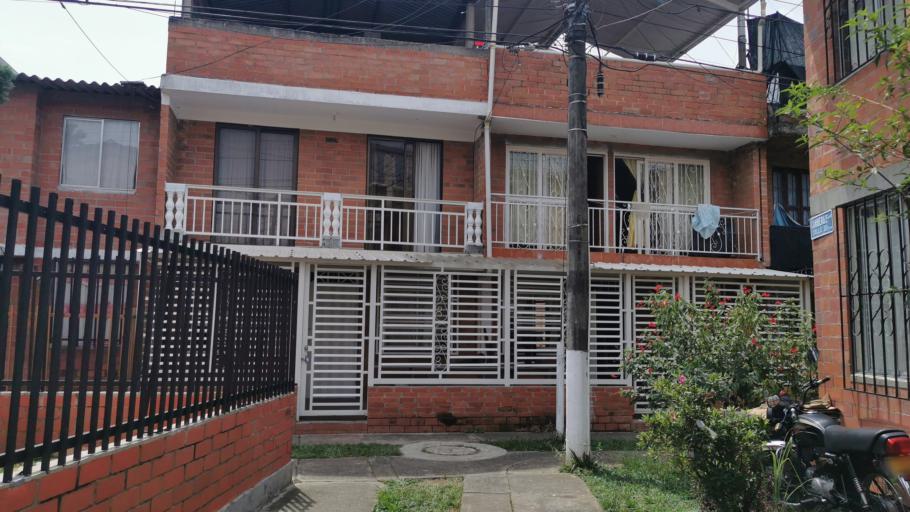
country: CO
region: Valle del Cauca
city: Jamundi
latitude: 3.2531
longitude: -76.5364
